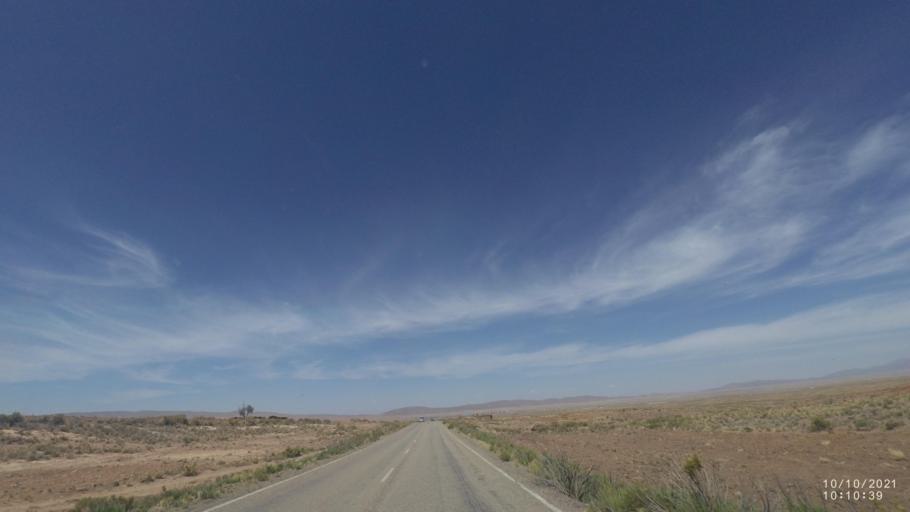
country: BO
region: La Paz
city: Eucaliptus
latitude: -17.4130
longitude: -67.4943
